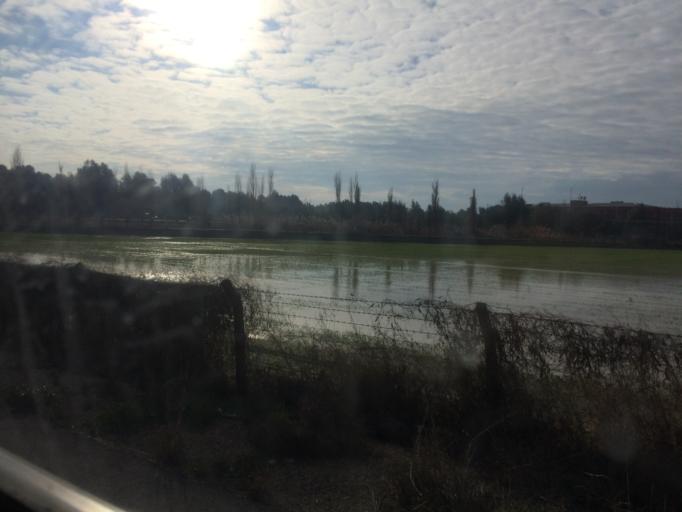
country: TR
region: Izmir
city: Karsiyaka
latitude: 38.4943
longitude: 26.9602
